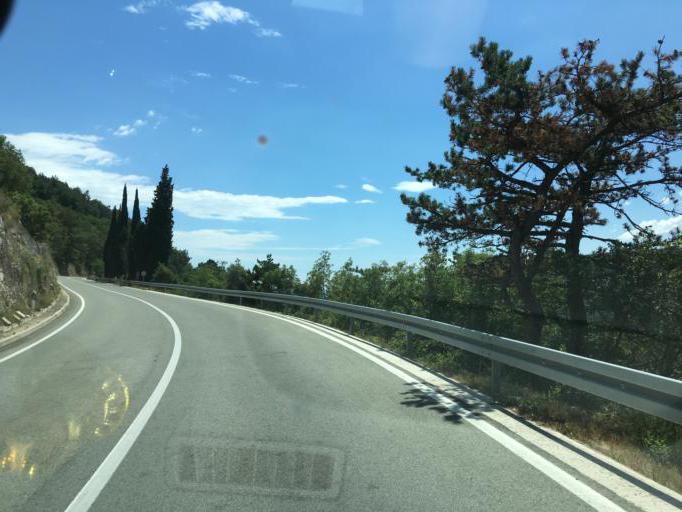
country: HR
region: Istarska
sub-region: Grad Labin
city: Rabac
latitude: 45.1359
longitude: 14.1839
